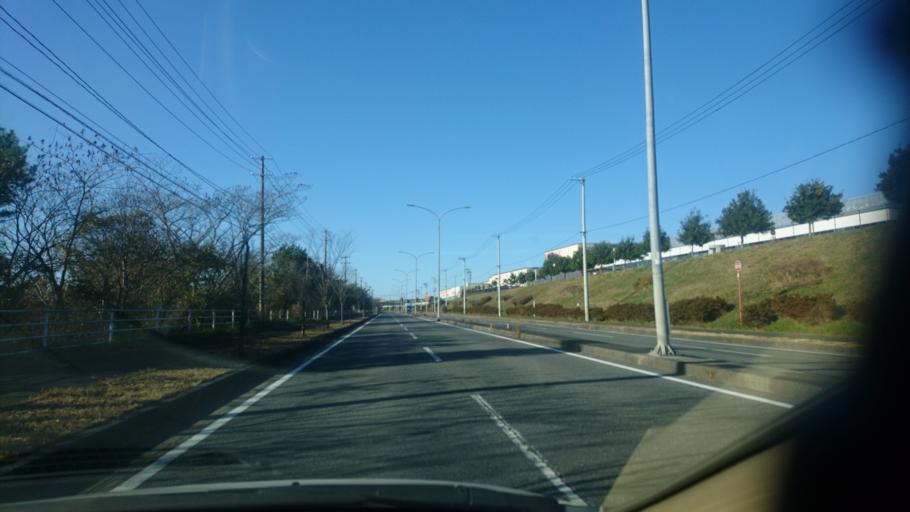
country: JP
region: Miyagi
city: Tomiya
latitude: 38.4549
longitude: 140.9318
